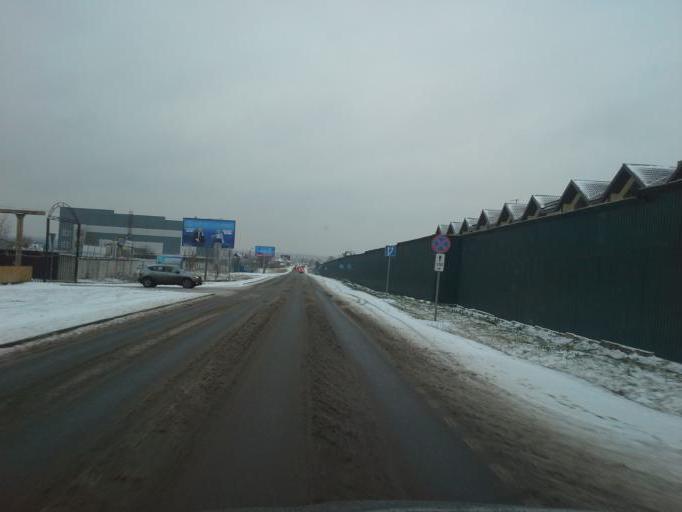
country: RU
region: Moskovskaya
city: Gorki Vtoryye
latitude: 55.7518
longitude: 37.1219
